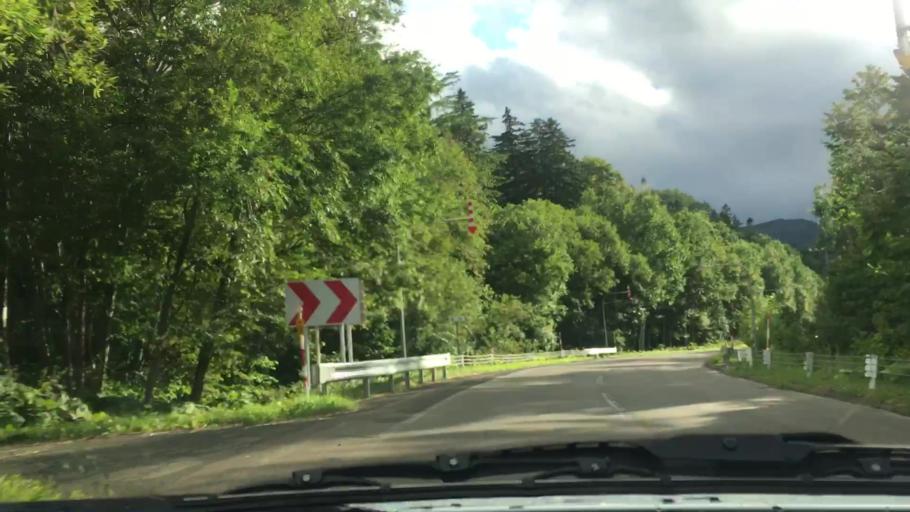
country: JP
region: Hokkaido
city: Shimo-furano
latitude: 43.0866
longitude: 142.6782
